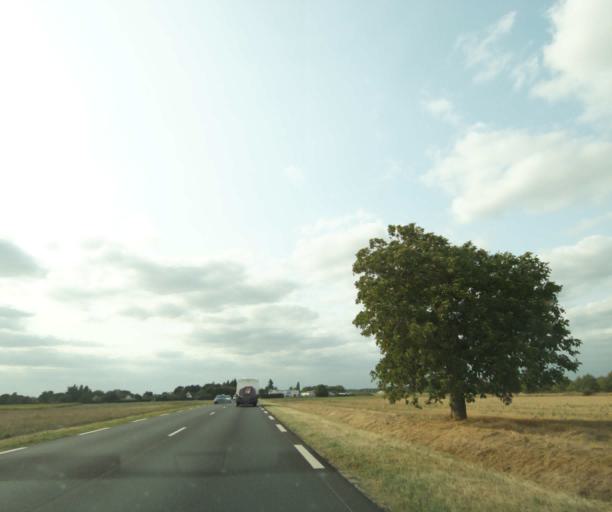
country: FR
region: Centre
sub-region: Departement d'Indre-et-Loire
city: Esvres
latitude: 47.2903
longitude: 0.8109
